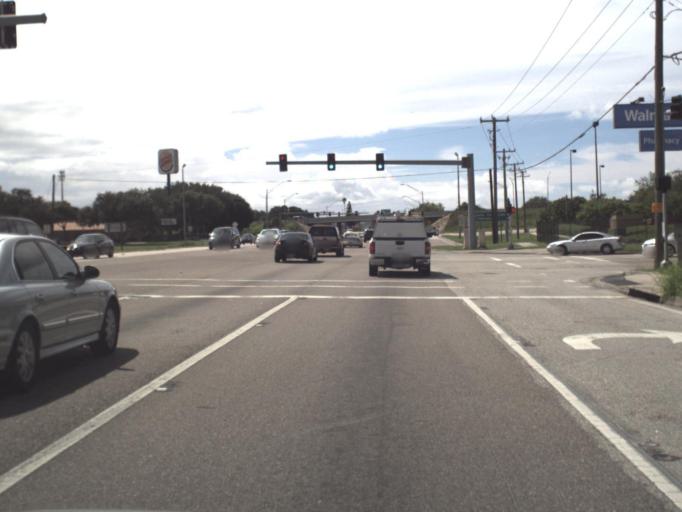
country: US
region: Florida
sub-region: Manatee County
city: Palmetto
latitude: 27.5213
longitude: -82.5589
